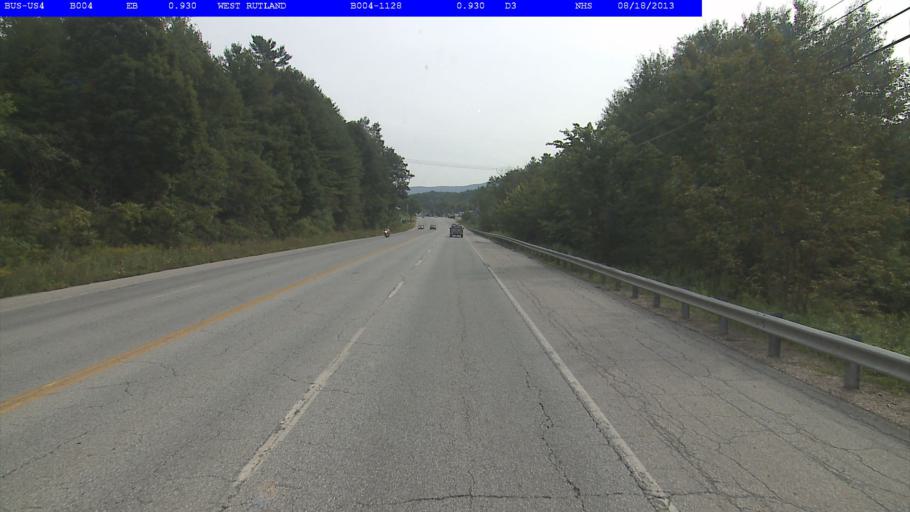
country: US
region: Vermont
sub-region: Rutland County
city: West Rutland
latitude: 43.5940
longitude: -73.0314
